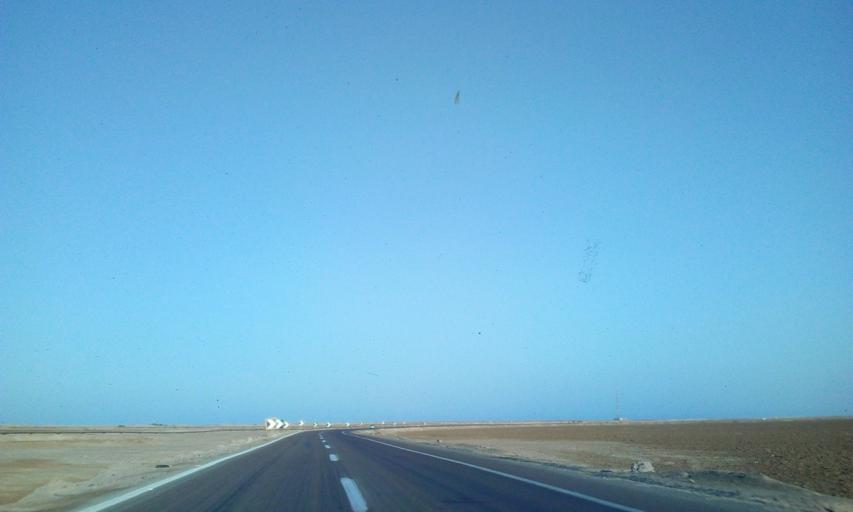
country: EG
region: South Sinai
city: Tor
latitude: 28.2703
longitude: 33.1451
